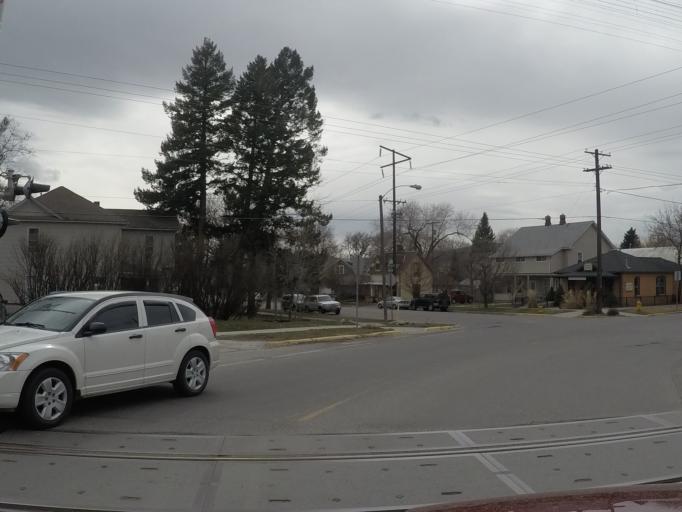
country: US
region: Montana
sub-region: Missoula County
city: Missoula
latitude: 46.8720
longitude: -113.9853
